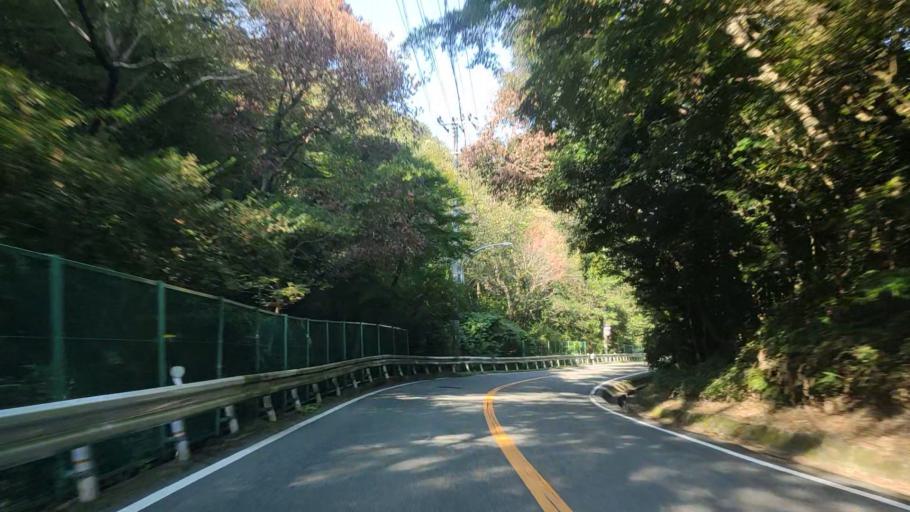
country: JP
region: Hyogo
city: Sandacho
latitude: 34.7982
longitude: 135.2395
